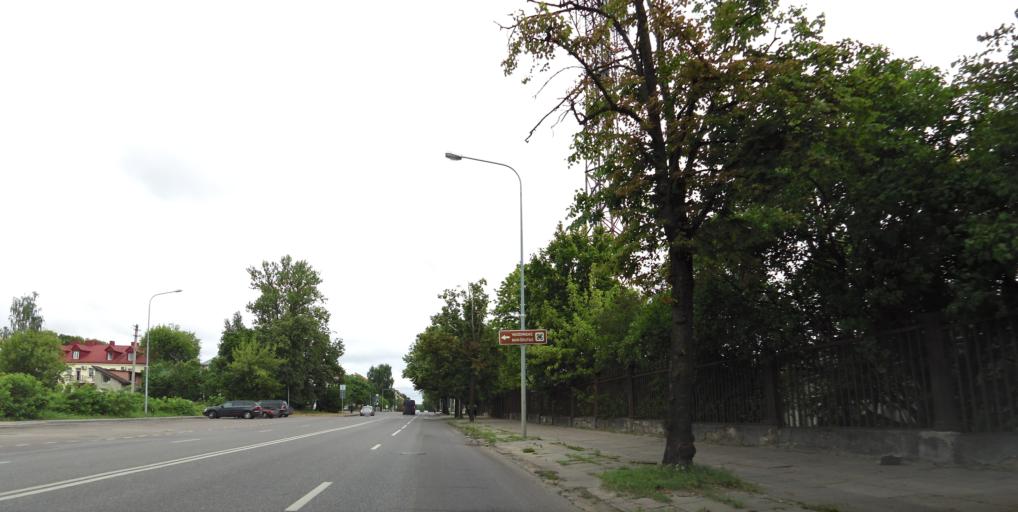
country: LT
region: Vilnius County
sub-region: Vilnius
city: Vilnius
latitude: 54.6936
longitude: 25.2888
